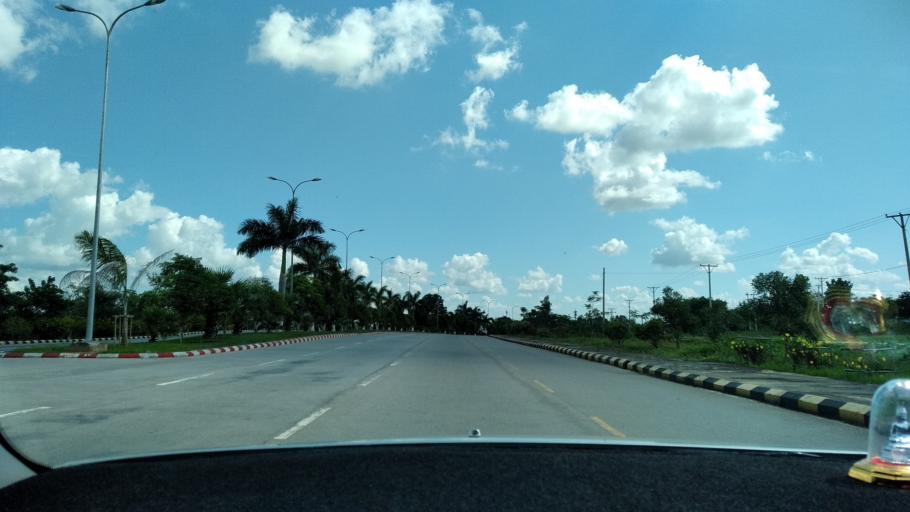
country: MM
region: Mandalay
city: Nay Pyi Taw
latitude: 19.7775
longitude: 96.1429
